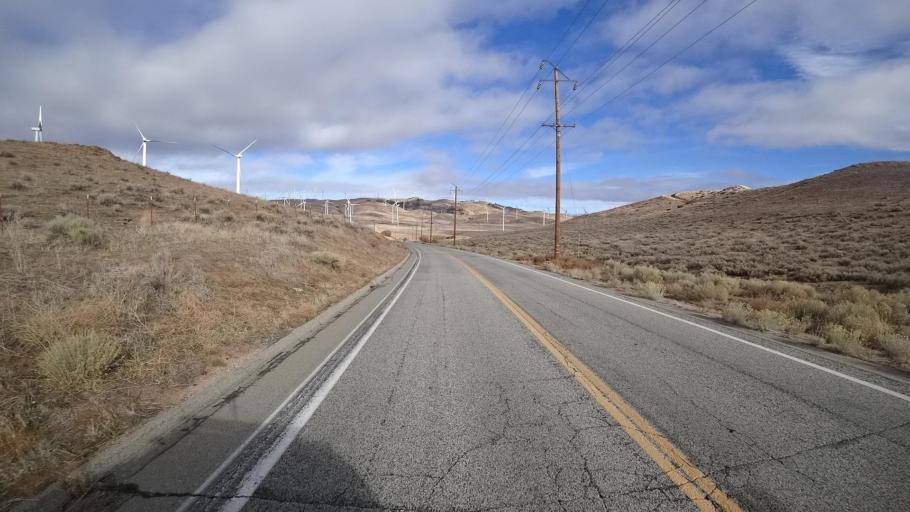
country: US
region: California
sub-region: Kern County
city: Tehachapi
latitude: 35.0441
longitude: -118.3534
